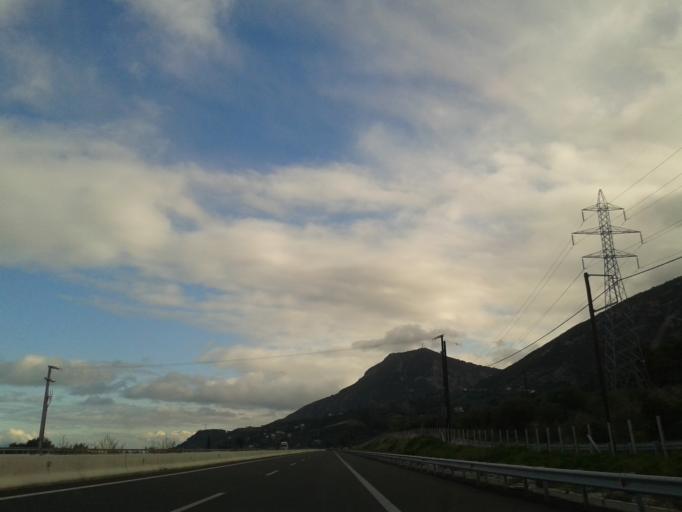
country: GR
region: Peloponnese
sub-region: Nomos Korinthias
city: Xylokastro
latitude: 38.1106
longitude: 22.5246
